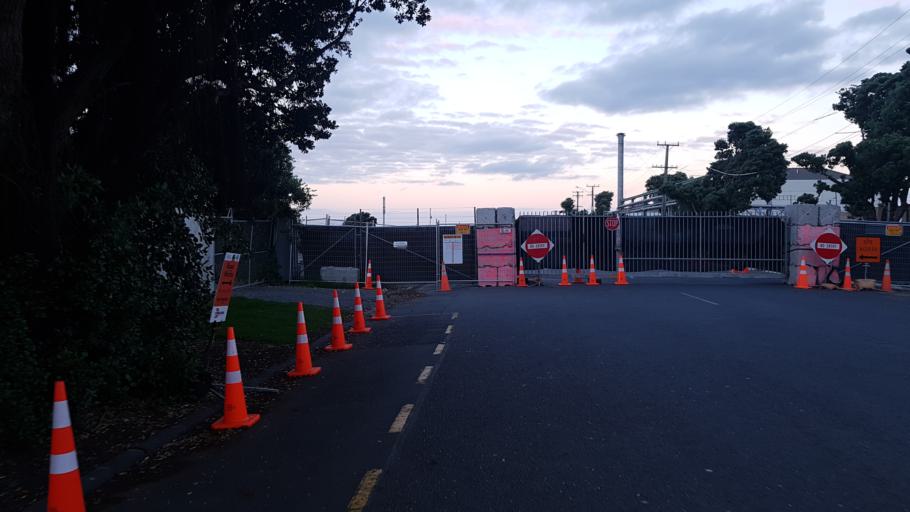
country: NZ
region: Auckland
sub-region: Auckland
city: Auckland
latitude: -36.8378
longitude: 174.7571
